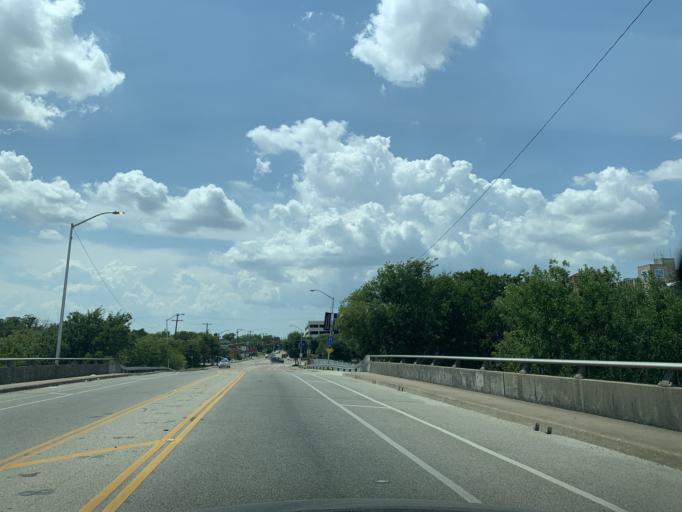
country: US
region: Texas
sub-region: Tarrant County
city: Fort Worth
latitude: 32.7260
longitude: -97.3246
